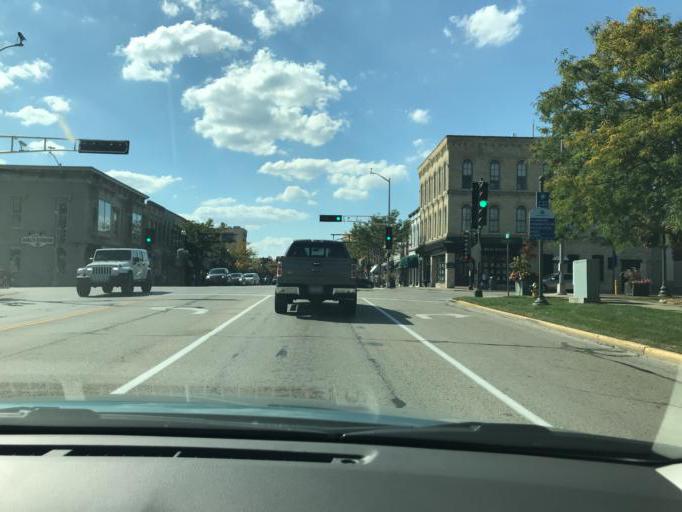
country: US
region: Wisconsin
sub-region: Walworth County
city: Lake Geneva
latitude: 42.5918
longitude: -88.4332
